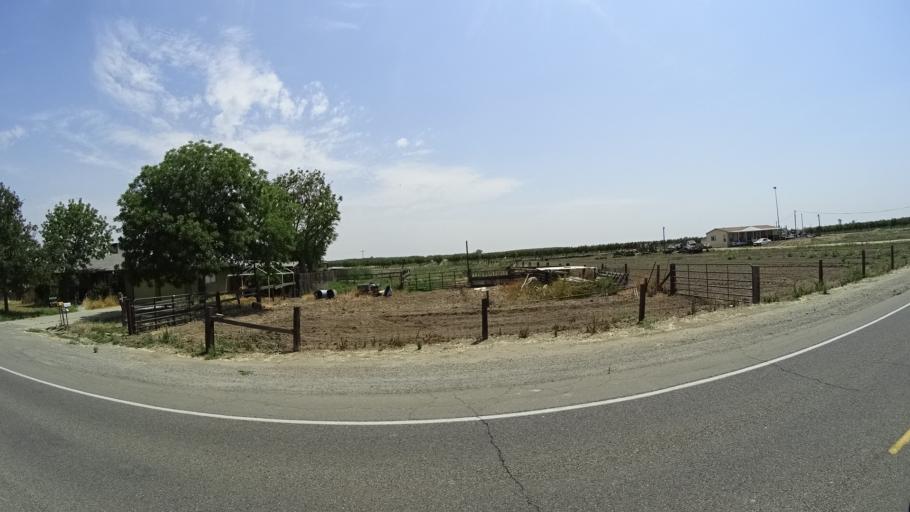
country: US
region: California
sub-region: Kings County
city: Lemoore
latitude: 36.3386
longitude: -119.7808
